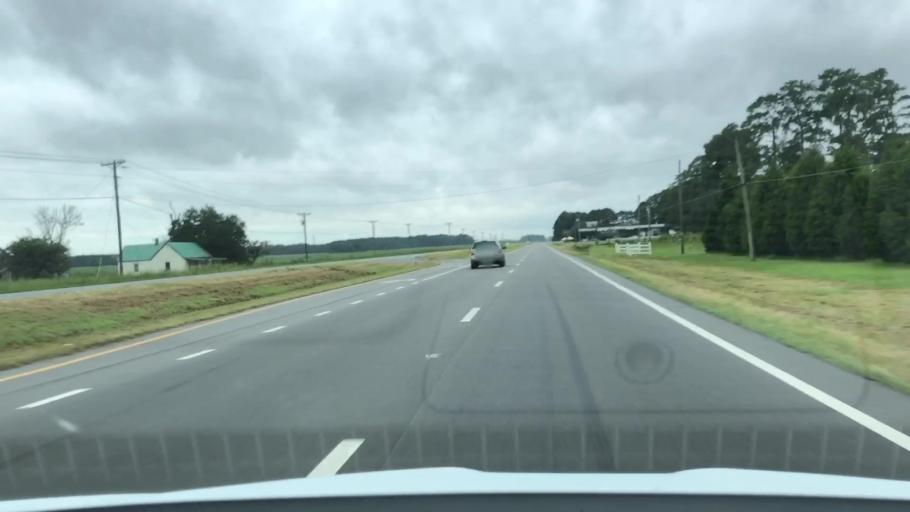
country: US
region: North Carolina
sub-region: Lenoir County
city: La Grange
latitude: 35.2600
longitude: -77.7036
